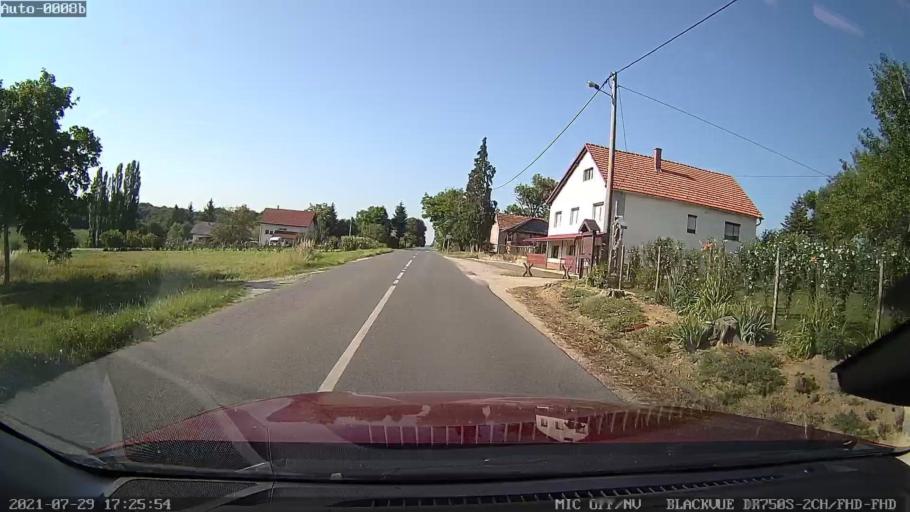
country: HR
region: Varazdinska
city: Ivanec
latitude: 46.2501
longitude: 16.1181
